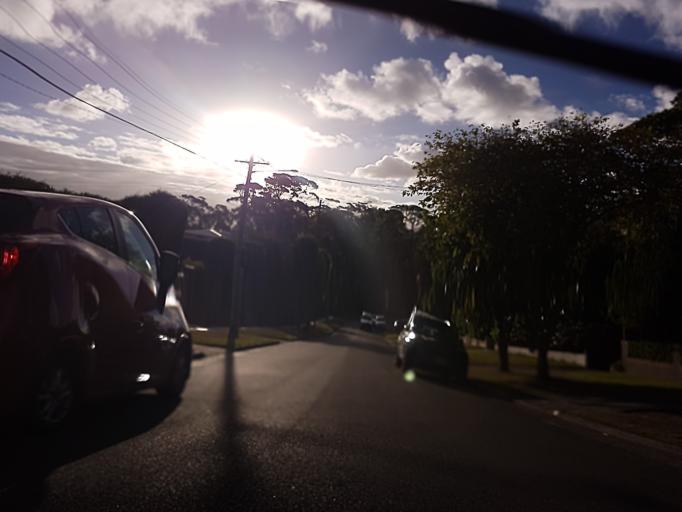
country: AU
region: New South Wales
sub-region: Manly Vale
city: Balgowlah
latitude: -33.7966
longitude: 151.2432
